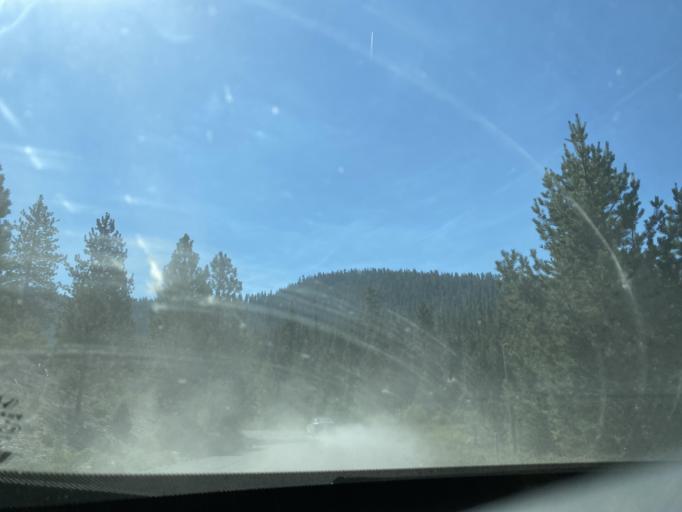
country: US
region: Oregon
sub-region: Deschutes County
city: Deschutes River Woods
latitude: 44.0332
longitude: -121.5236
